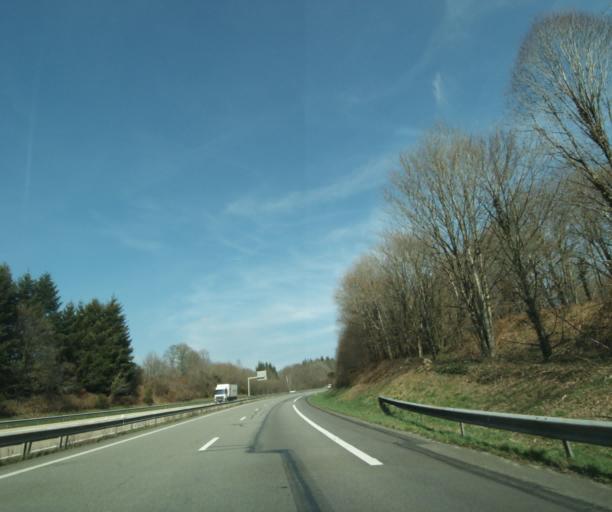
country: FR
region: Limousin
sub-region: Departement de la Haute-Vienne
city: Razes
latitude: 45.9892
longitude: 1.3254
